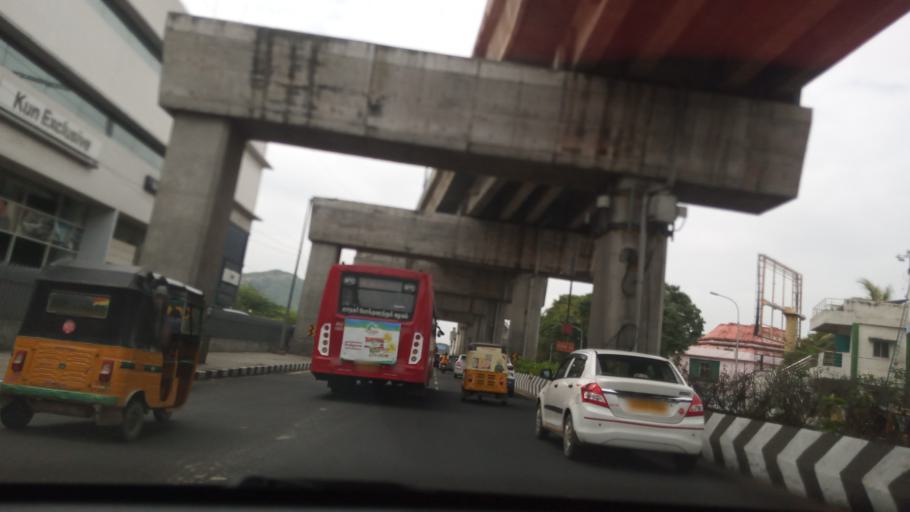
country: IN
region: Tamil Nadu
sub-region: Kancheepuram
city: Manappakkam
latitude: 12.9859
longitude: 80.1740
